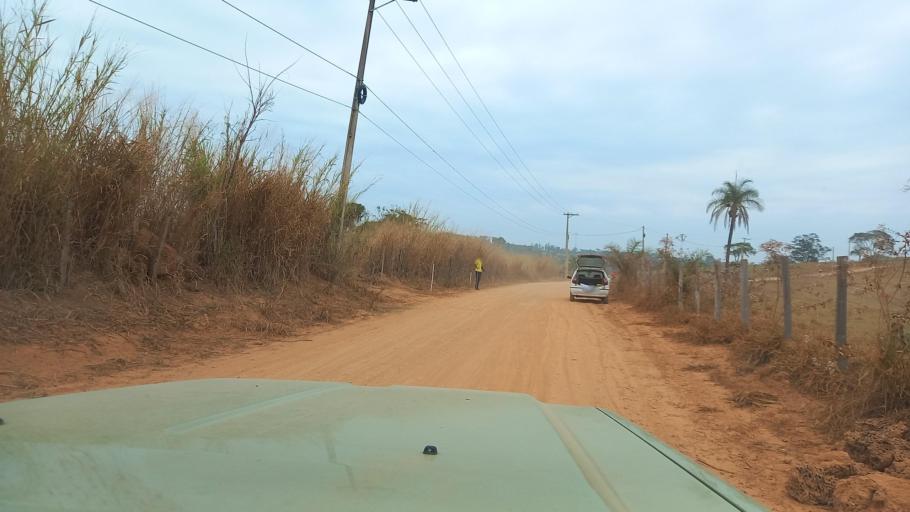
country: BR
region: Sao Paulo
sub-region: Moji-Guacu
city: Mogi-Gaucu
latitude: -22.3129
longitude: -46.8386
